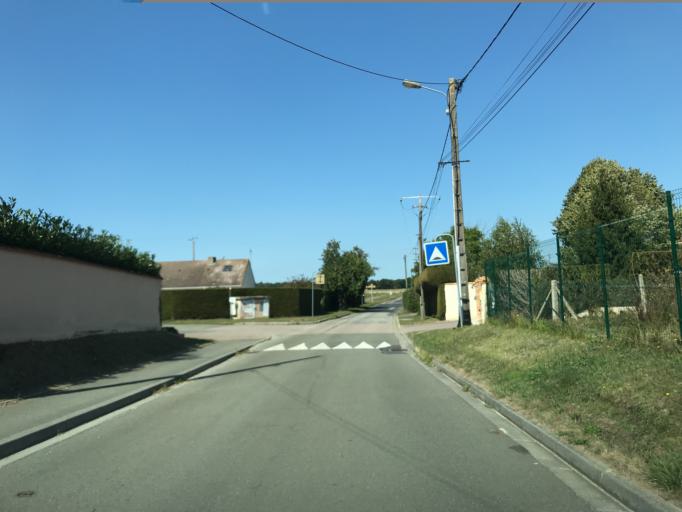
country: FR
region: Haute-Normandie
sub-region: Departement de l'Eure
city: Heudreville-sur-Eure
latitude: 49.0970
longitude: 1.2041
